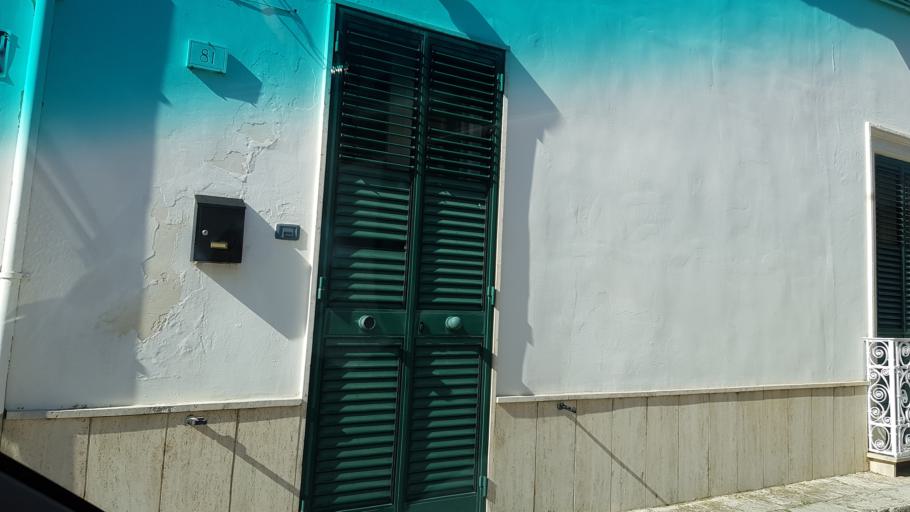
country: IT
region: Apulia
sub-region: Provincia di Lecce
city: Squinzano
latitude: 40.4385
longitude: 18.0430
